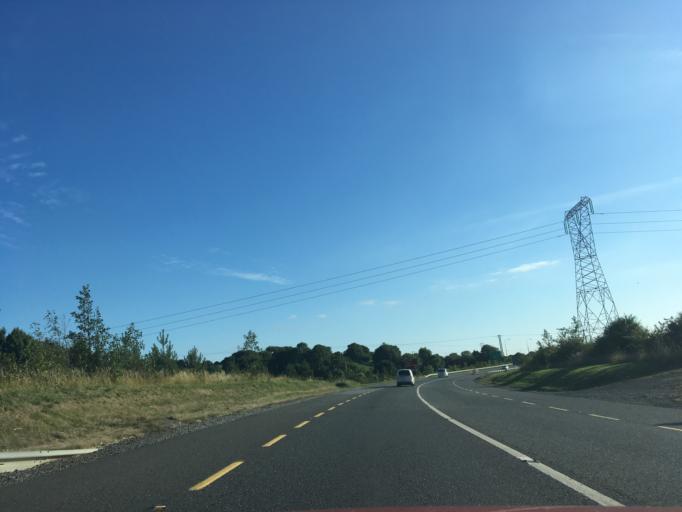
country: IE
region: Munster
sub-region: Waterford
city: Waterford
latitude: 52.2941
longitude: -7.0558
